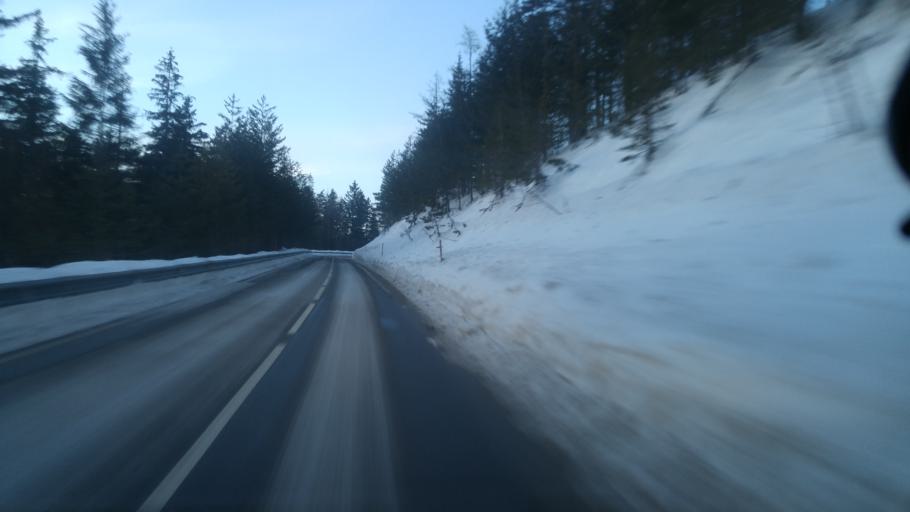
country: AT
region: Lower Austria
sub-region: Politischer Bezirk Wiener Neustadt
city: Rohr im Gebirge
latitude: 47.8697
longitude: 15.7929
